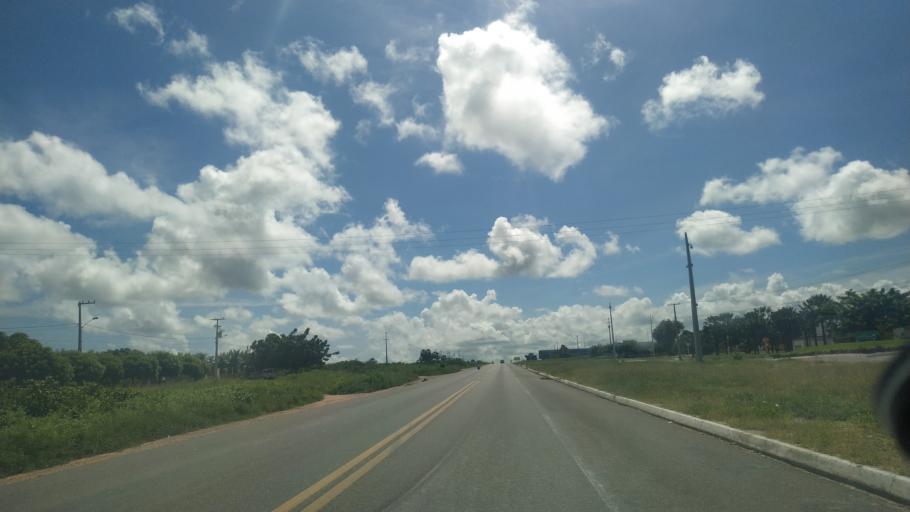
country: BR
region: Rio Grande do Norte
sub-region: Mossoro
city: Mossoro
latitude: -5.1873
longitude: -37.3041
